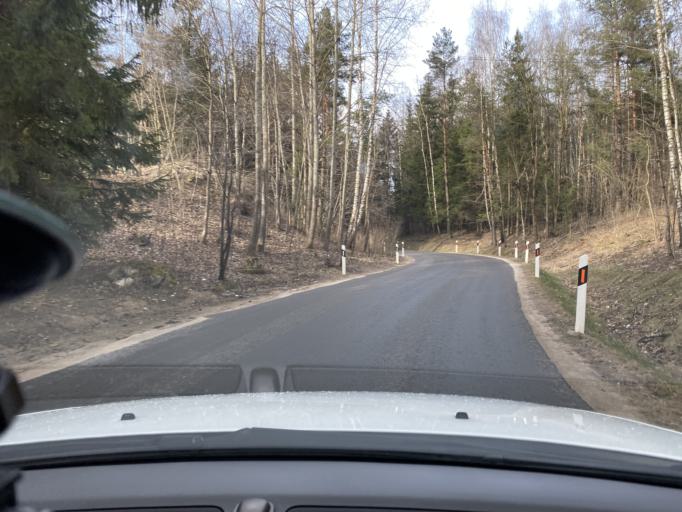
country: LT
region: Vilnius County
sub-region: Vilnius
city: Fabijoniskes
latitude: 54.7594
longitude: 25.2548
